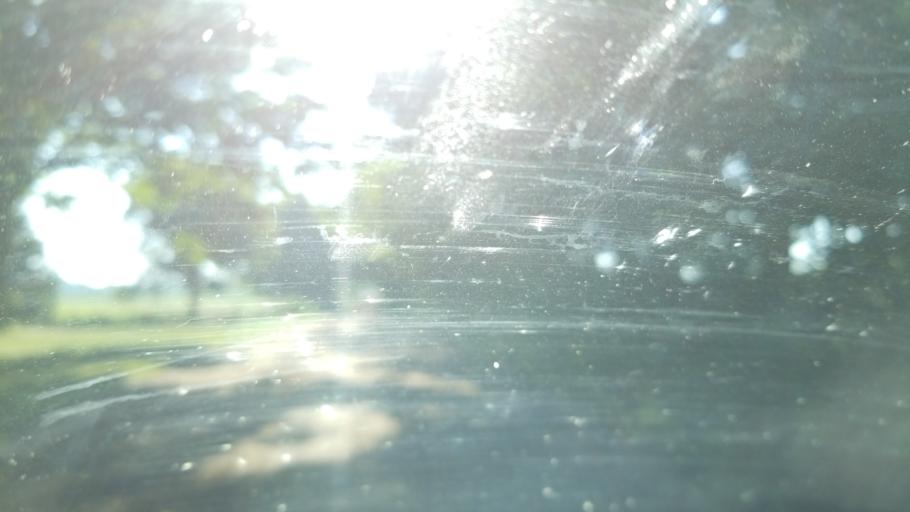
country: US
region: Michigan
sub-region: Mecosta County
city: Canadian Lakes
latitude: 43.5689
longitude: -85.3582
